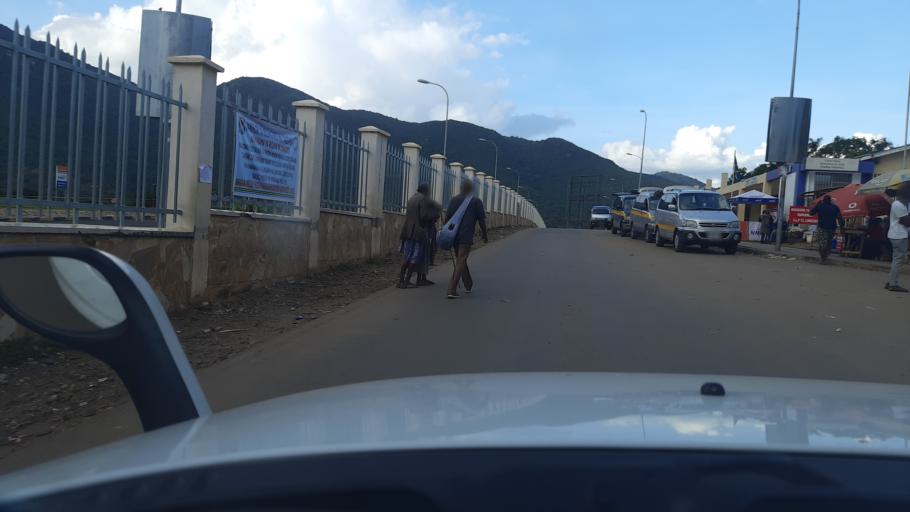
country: TZ
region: Arusha
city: Namanga
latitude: -2.5491
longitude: 36.7858
